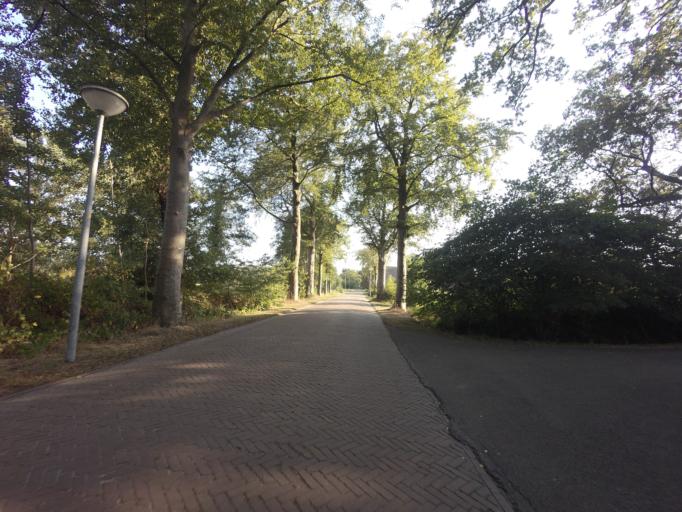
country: NL
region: Groningen
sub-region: Gemeente Groningen
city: Groningen
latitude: 53.1407
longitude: 6.4889
